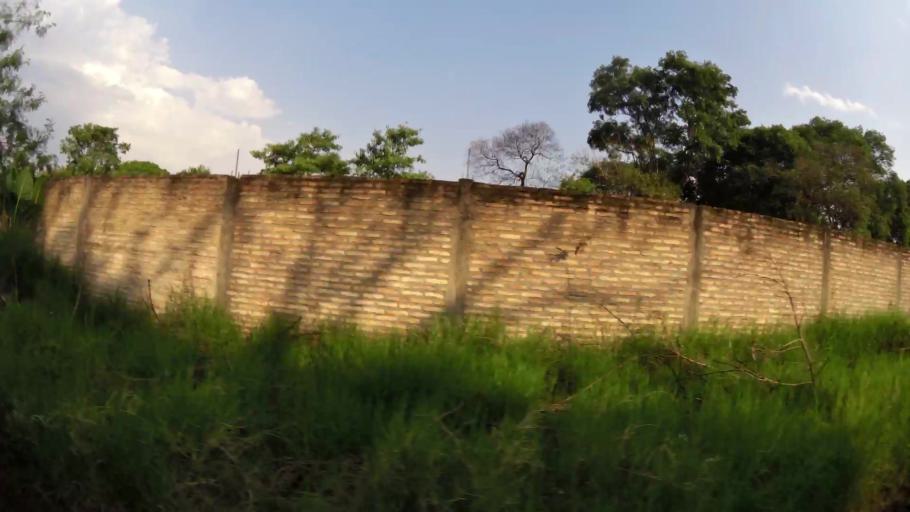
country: PY
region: Alto Parana
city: Presidente Franco
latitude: -25.5269
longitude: -54.6289
